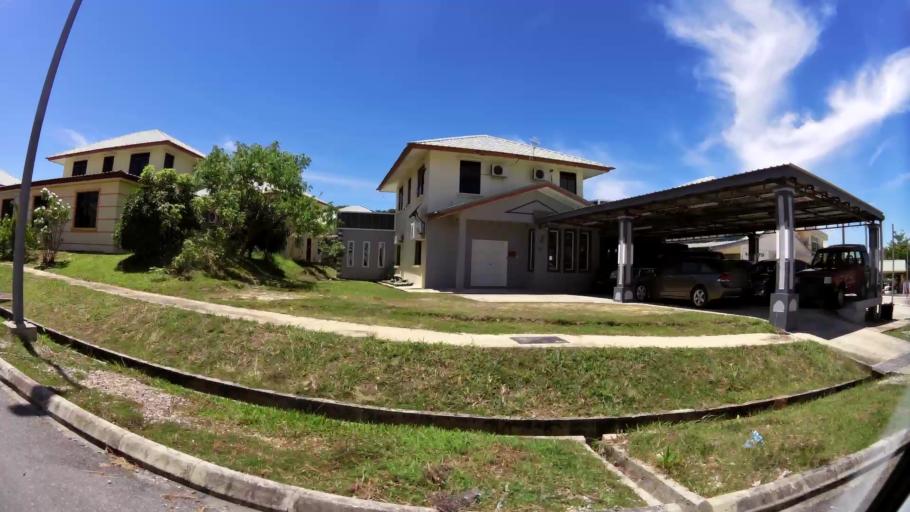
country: BN
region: Brunei and Muara
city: Bandar Seri Begawan
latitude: 5.0322
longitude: 115.0398
